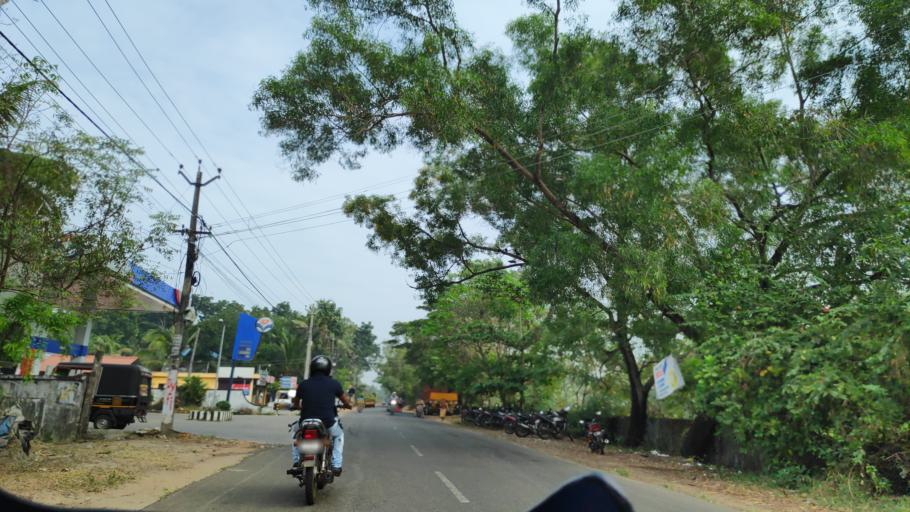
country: IN
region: Kerala
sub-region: Kottayam
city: Vaikam
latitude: 9.7553
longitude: 76.3631
